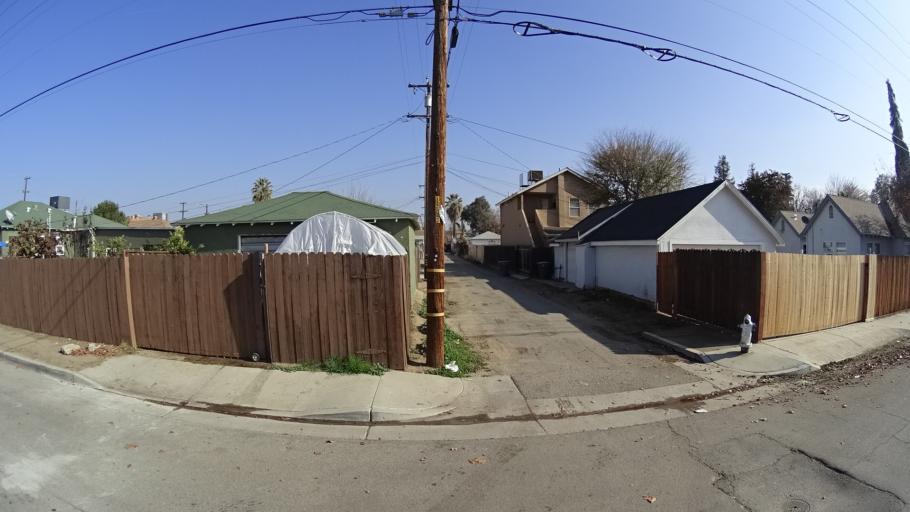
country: US
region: California
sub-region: Kern County
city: Bakersfield
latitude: 35.3898
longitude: -118.9991
